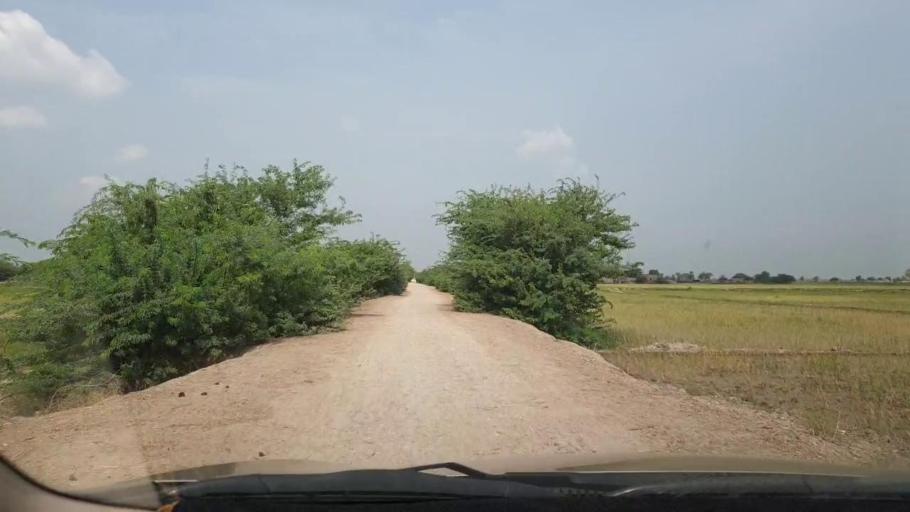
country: PK
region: Sindh
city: Larkana
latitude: 27.5084
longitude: 68.1365
